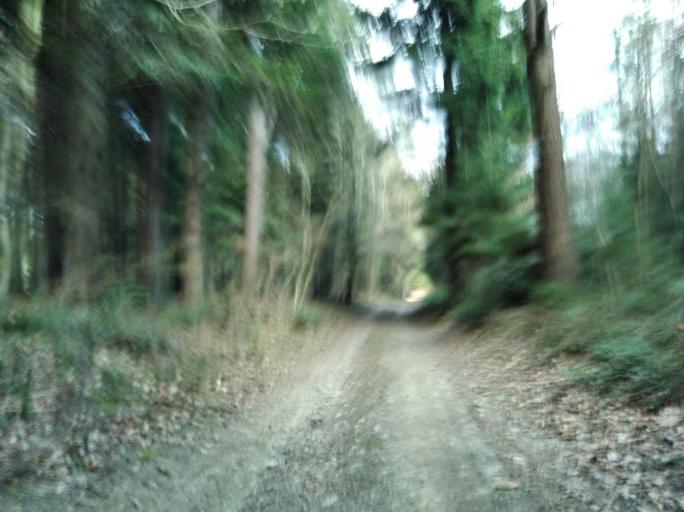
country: PL
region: Subcarpathian Voivodeship
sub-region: Powiat strzyzowski
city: Strzyzow
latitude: 49.8279
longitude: 21.8047
